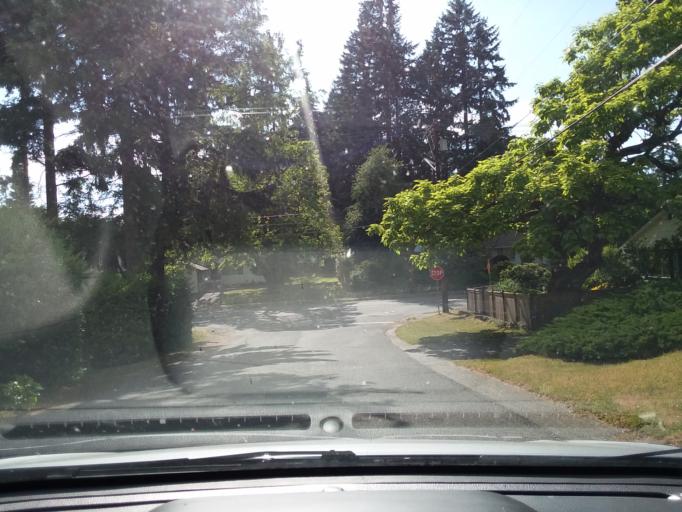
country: US
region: Washington
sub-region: Snohomish County
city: Mountlake Terrace
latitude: 47.7911
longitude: -122.3215
